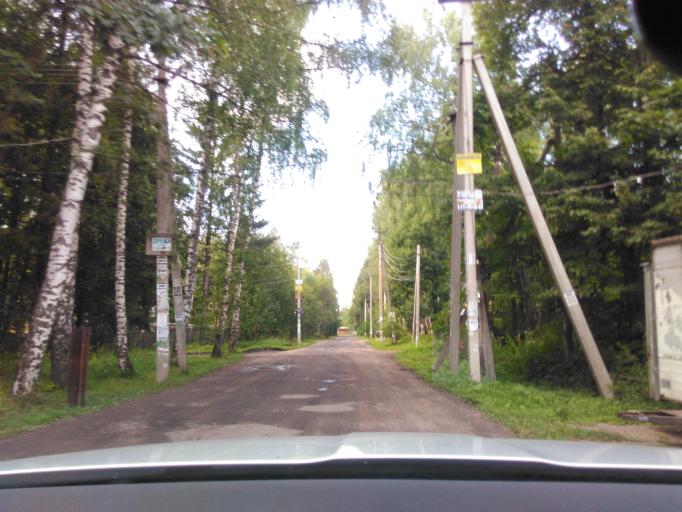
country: RU
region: Moskovskaya
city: Radumlya
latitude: 56.1295
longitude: 37.2128
